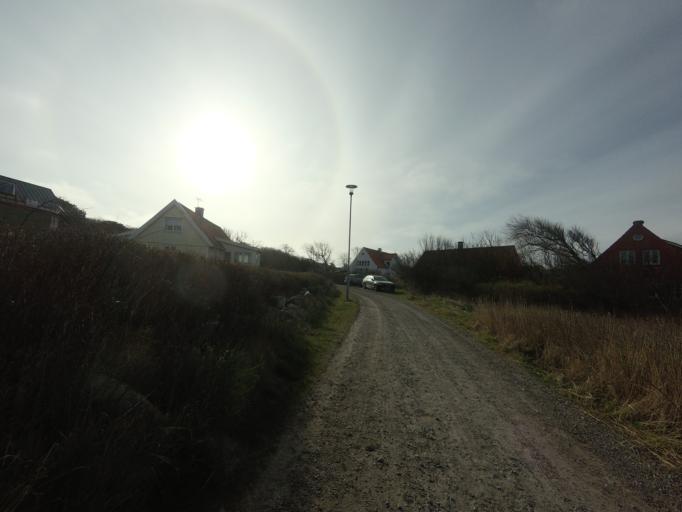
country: SE
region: Skane
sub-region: Hoganas Kommun
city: Hoganas
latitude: 56.2587
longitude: 12.5200
